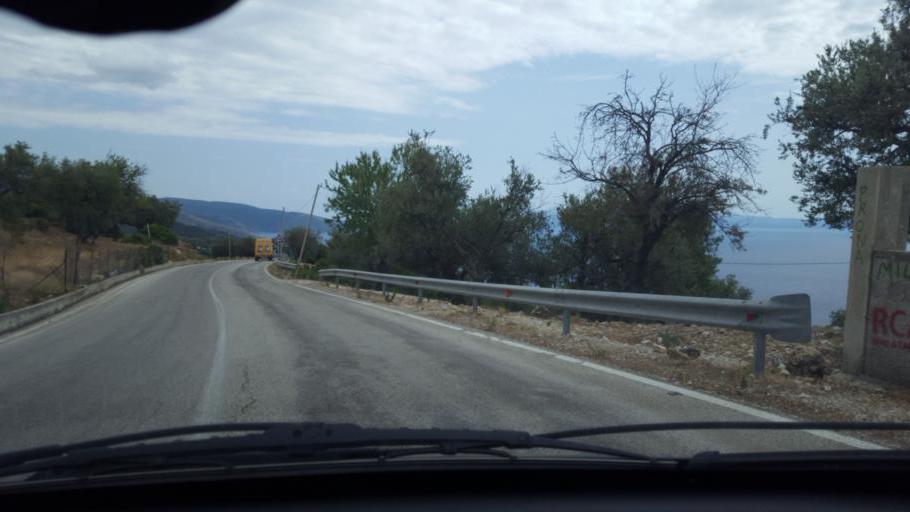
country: AL
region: Vlore
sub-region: Rrethi i Sarandes
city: Lukove
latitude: 40.0258
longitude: 19.8839
